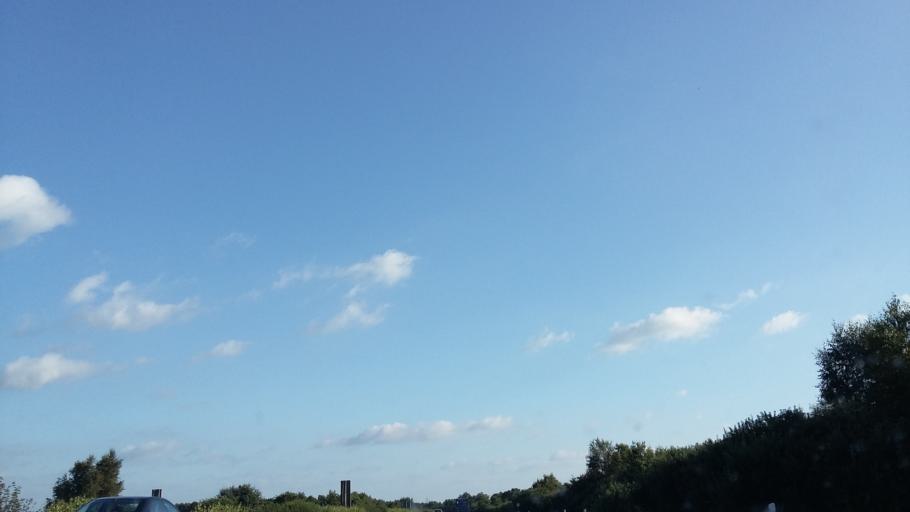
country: DE
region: Lower Saxony
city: Schiffdorf
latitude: 53.5452
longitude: 8.6194
